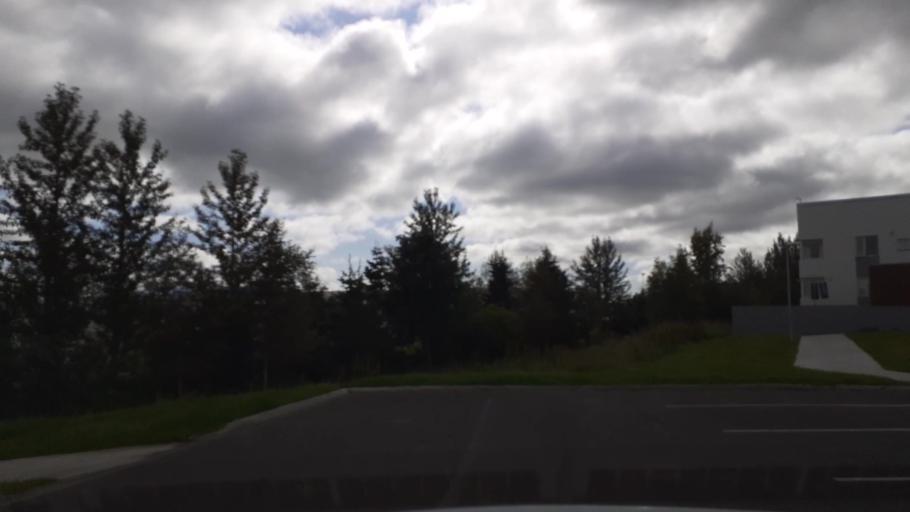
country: IS
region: Northeast
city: Akureyri
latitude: 65.6669
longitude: -18.0974
